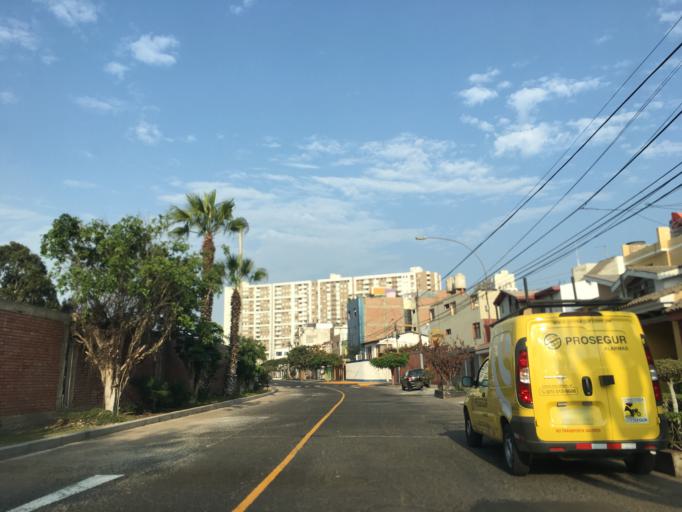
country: PE
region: Callao
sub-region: Callao
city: Callao
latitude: -12.0735
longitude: -77.0819
